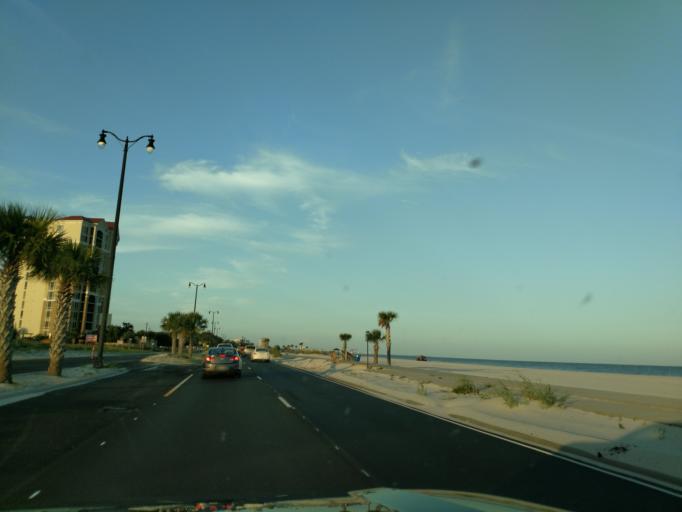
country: US
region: Mississippi
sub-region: Harrison County
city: Gulfport
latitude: 30.3811
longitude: -89.0304
